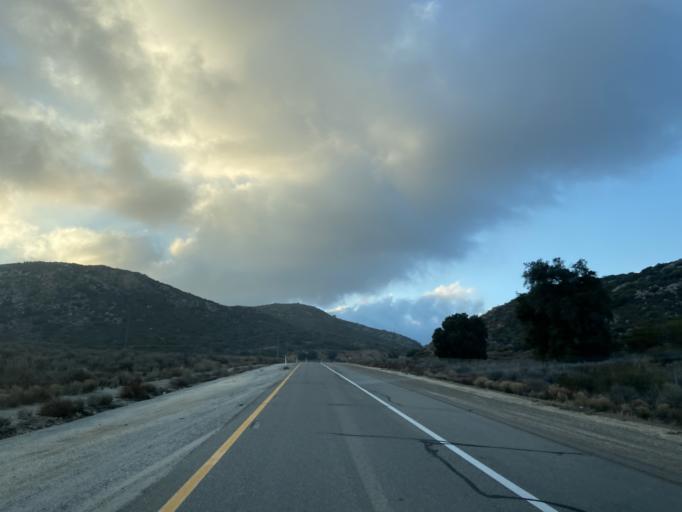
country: US
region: California
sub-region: San Diego County
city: Campo
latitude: 32.7195
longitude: -116.4706
